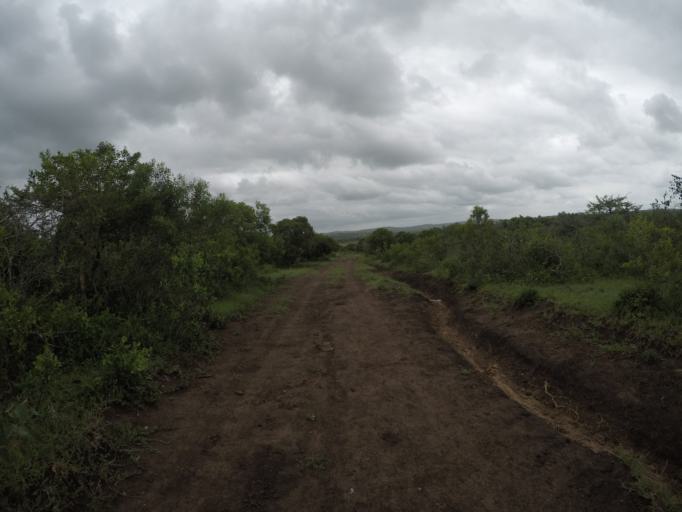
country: ZA
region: KwaZulu-Natal
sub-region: uThungulu District Municipality
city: Empangeni
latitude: -28.5687
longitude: 31.8720
